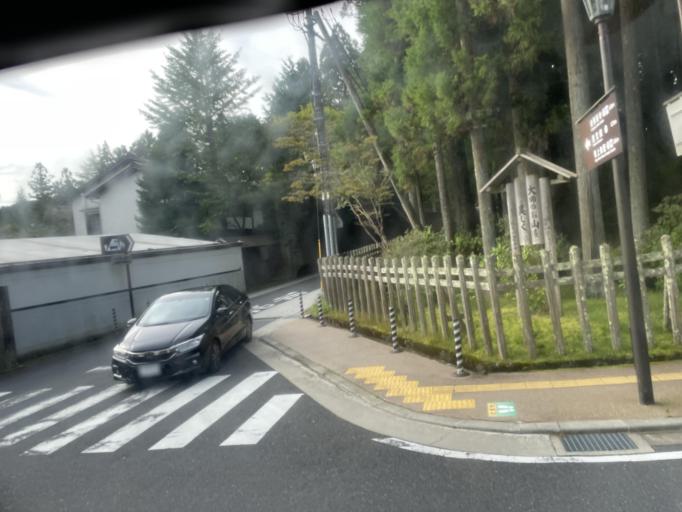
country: JP
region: Wakayama
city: Koya
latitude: 34.2155
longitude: 135.5852
